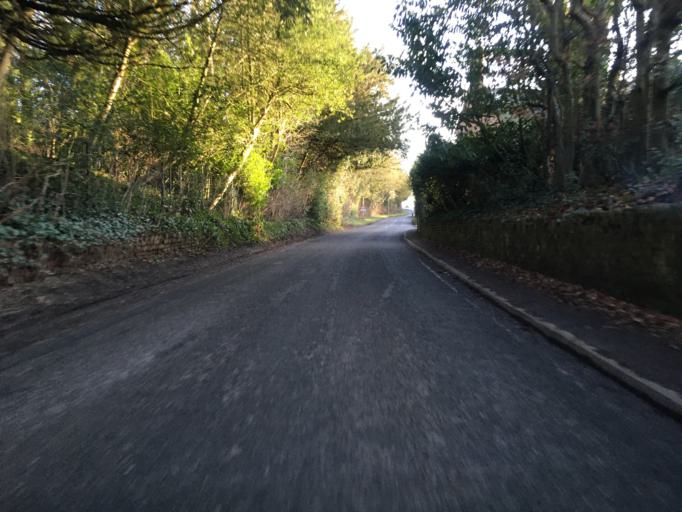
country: GB
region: England
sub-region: Warwickshire
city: Stratford-upon-Avon
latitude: 52.2343
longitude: -1.6860
